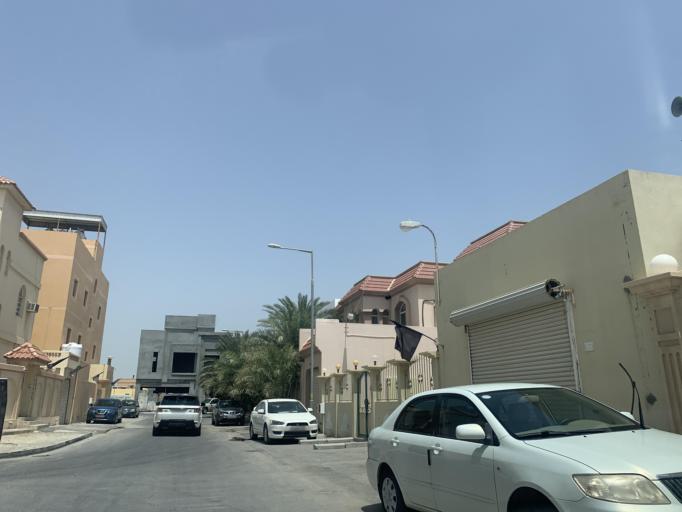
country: BH
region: Central Governorate
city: Madinat Hamad
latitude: 26.1460
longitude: 50.5047
